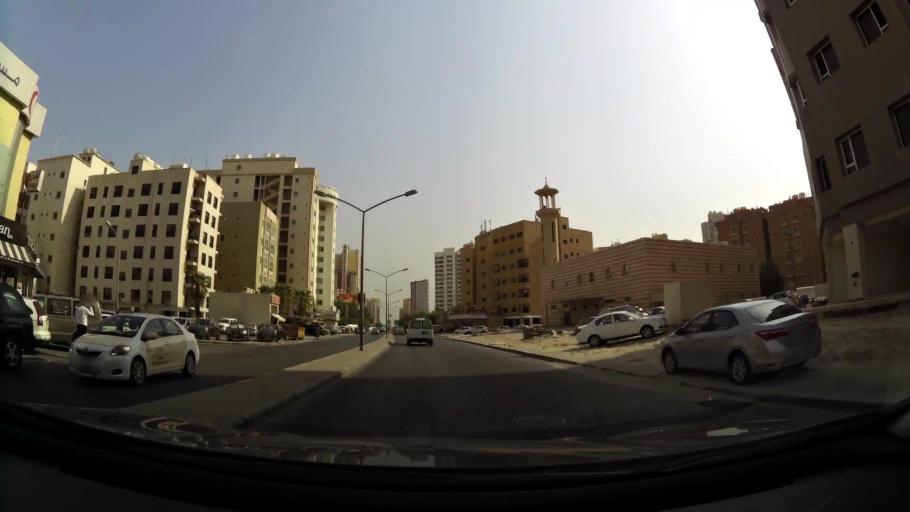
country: KW
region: Muhafazat Hawalli
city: As Salimiyah
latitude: 29.3284
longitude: 48.0557
